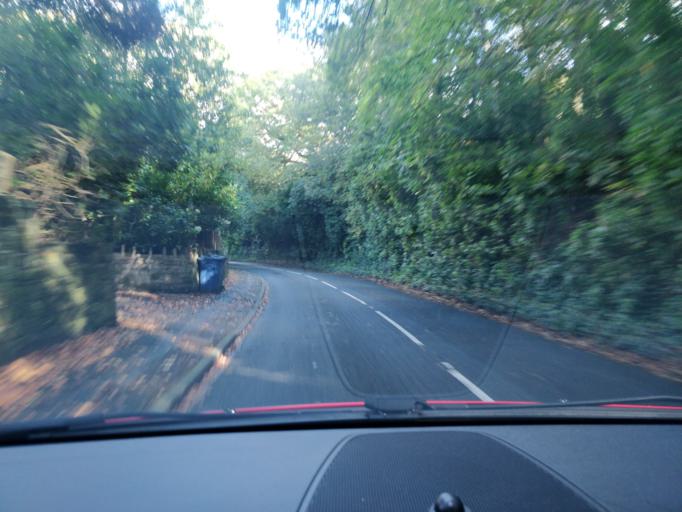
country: GB
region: England
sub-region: Lancashire
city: Ormskirk
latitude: 53.5718
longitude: -2.8670
